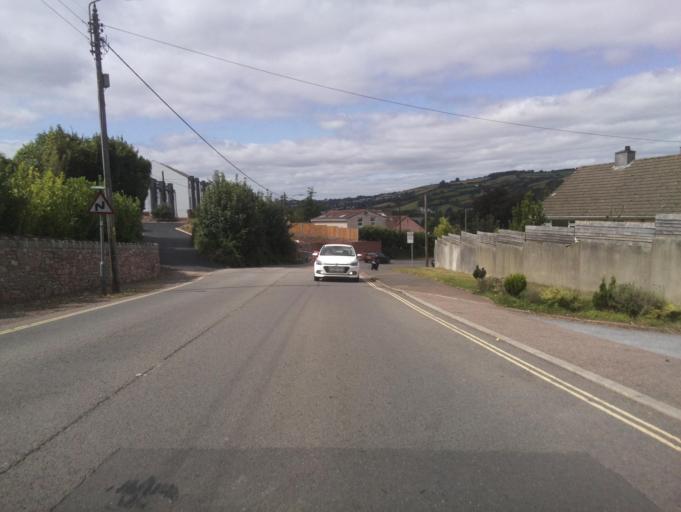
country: GB
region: England
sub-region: Devon
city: Teignmouth
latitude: 50.5392
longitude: -3.5103
